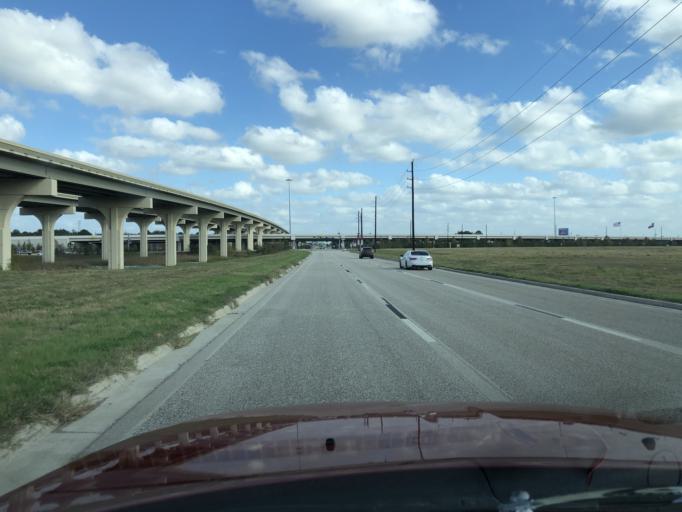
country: US
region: Texas
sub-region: Harris County
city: Tomball
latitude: 30.0514
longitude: -95.6188
